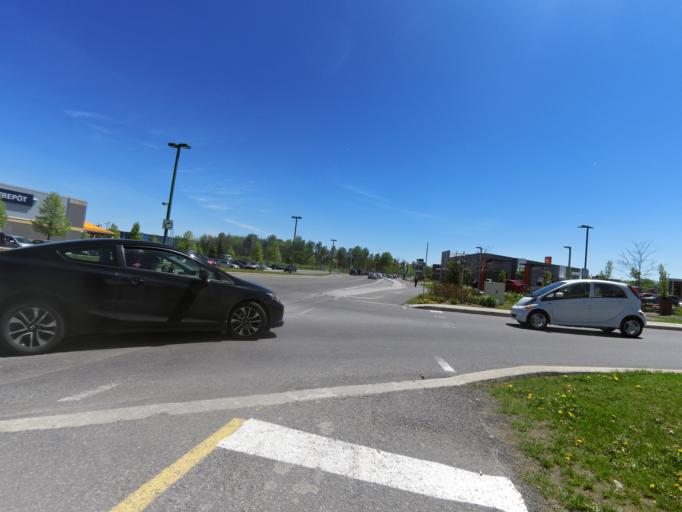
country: CA
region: Ontario
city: Ottawa
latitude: 45.4345
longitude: -75.7799
